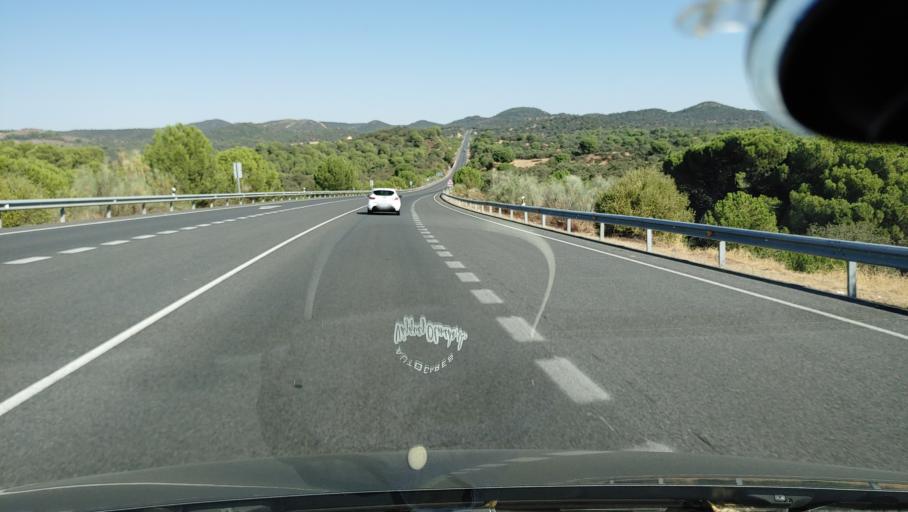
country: ES
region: Andalusia
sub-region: Province of Cordoba
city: Cordoba
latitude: 37.9988
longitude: -4.7972
